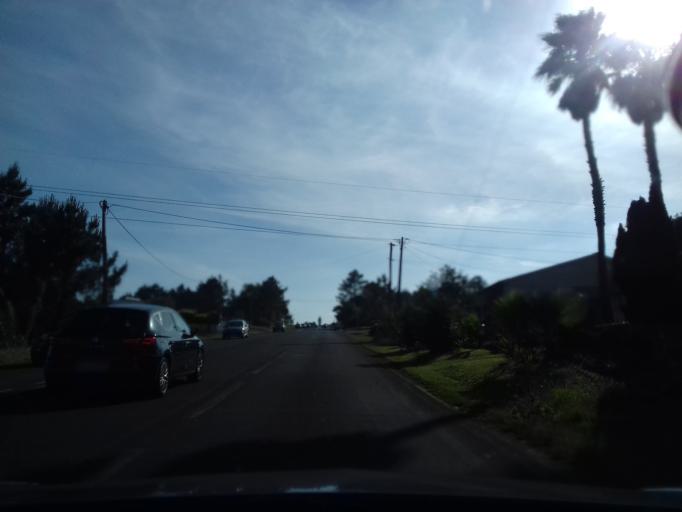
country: PT
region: Leiria
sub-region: Leiria
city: Leiria
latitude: 39.7135
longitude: -8.8378
